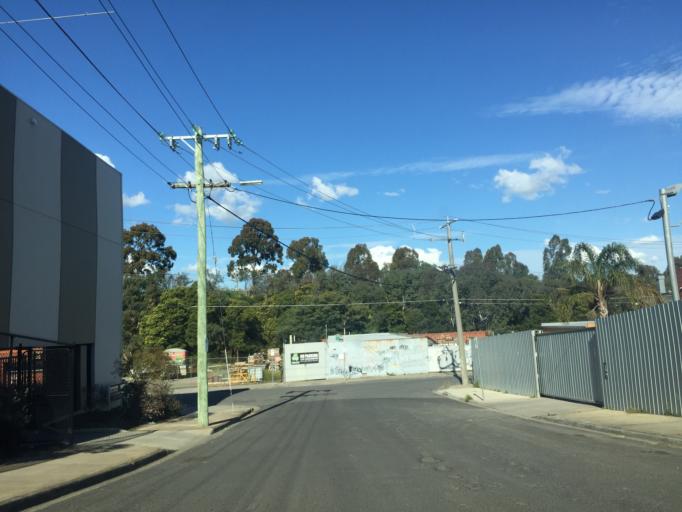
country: AU
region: Victoria
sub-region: Banyule
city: Bellfield
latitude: -37.7656
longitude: 145.0299
